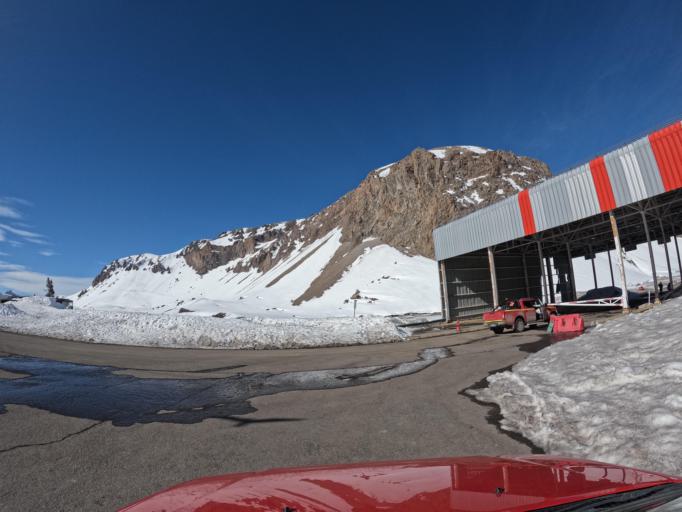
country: CL
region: Maule
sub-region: Provincia de Linares
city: Colbun
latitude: -36.0081
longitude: -70.5592
